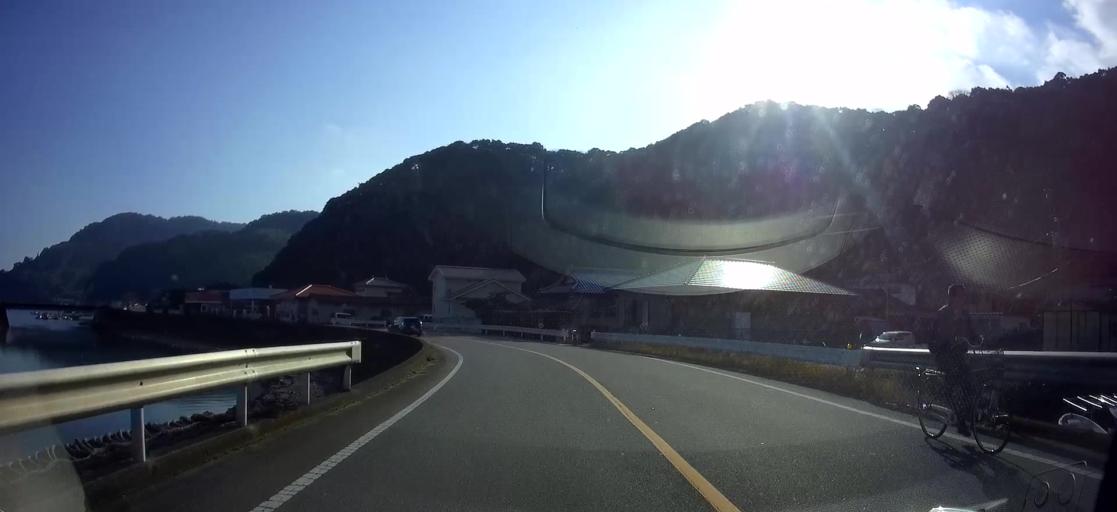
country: JP
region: Kumamoto
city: Hondo
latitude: 32.4271
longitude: 130.4018
